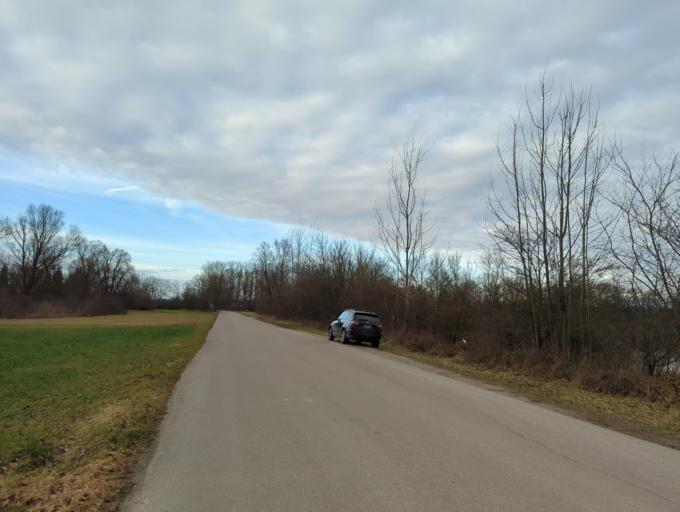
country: DE
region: Bavaria
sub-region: Swabia
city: Guenzburg
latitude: 48.4820
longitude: 10.3054
